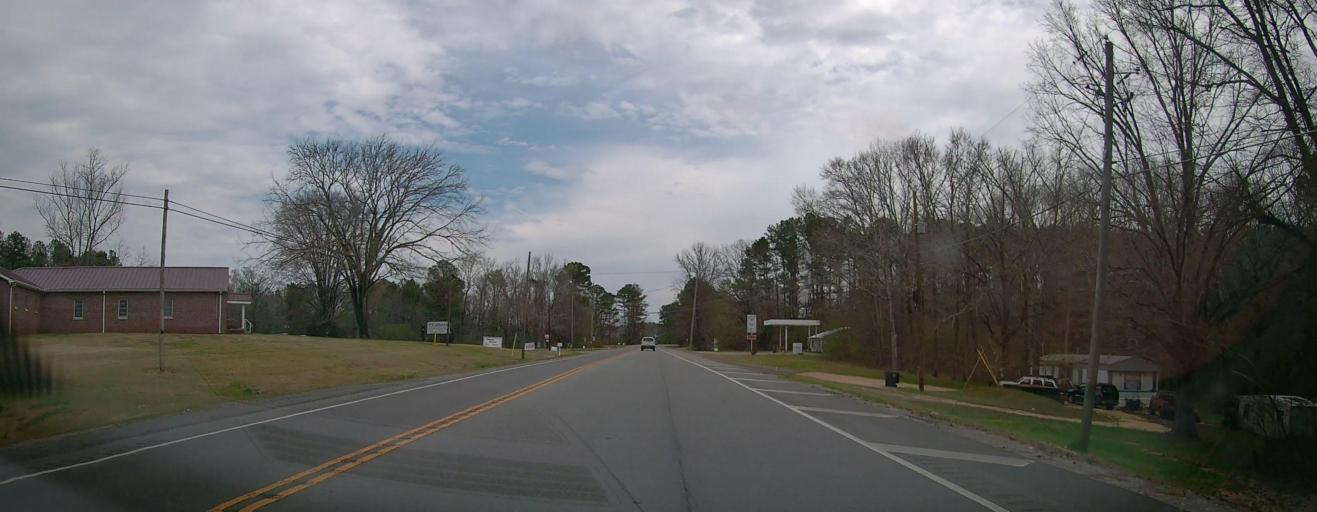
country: US
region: Alabama
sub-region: Marion County
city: Guin
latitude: 33.9872
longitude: -87.9219
